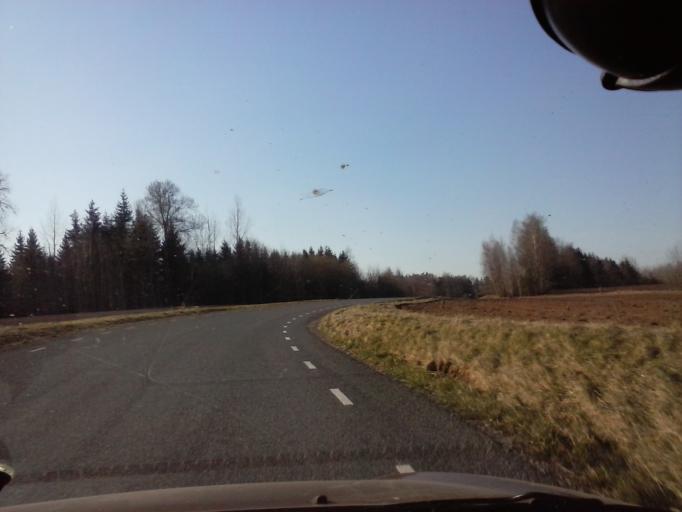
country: EE
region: Tartu
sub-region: UElenurme vald
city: Ulenurme
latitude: 58.1605
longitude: 26.8498
